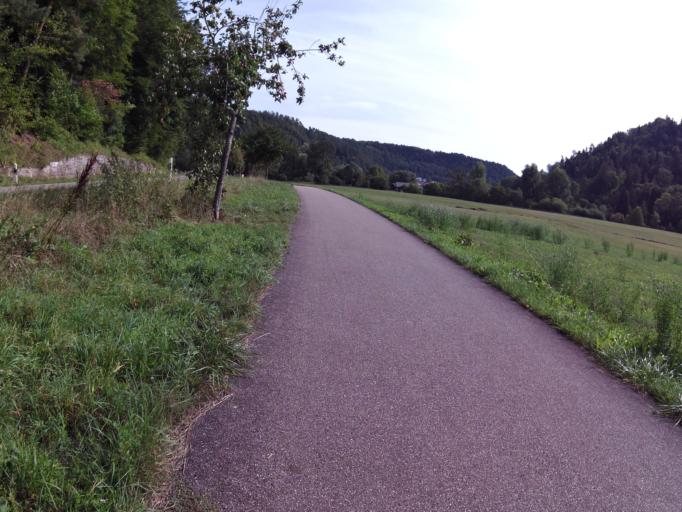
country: DE
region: Baden-Wuerttemberg
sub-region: Freiburg Region
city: Epfendorf
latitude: 48.2642
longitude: 8.6044
